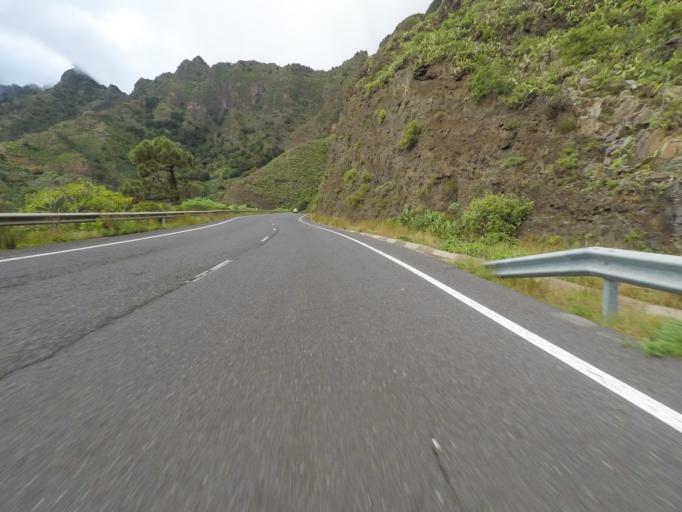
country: ES
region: Canary Islands
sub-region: Provincia de Santa Cruz de Tenerife
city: Hermigua
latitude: 28.1315
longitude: -17.1782
